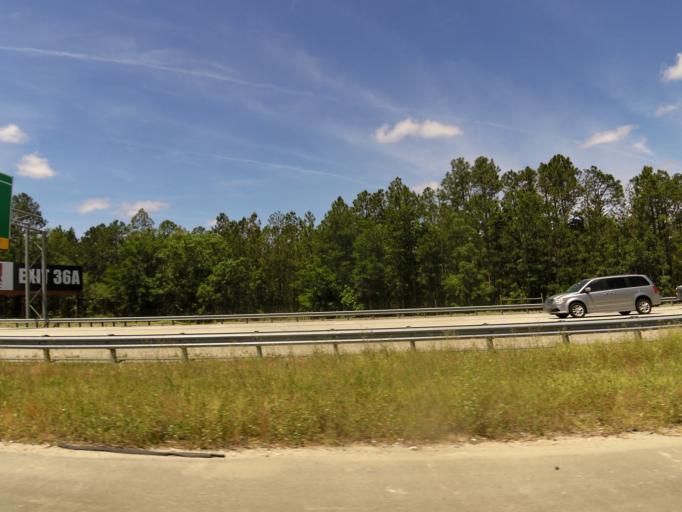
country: US
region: Georgia
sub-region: McIntosh County
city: Darien
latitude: 31.3174
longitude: -81.4761
